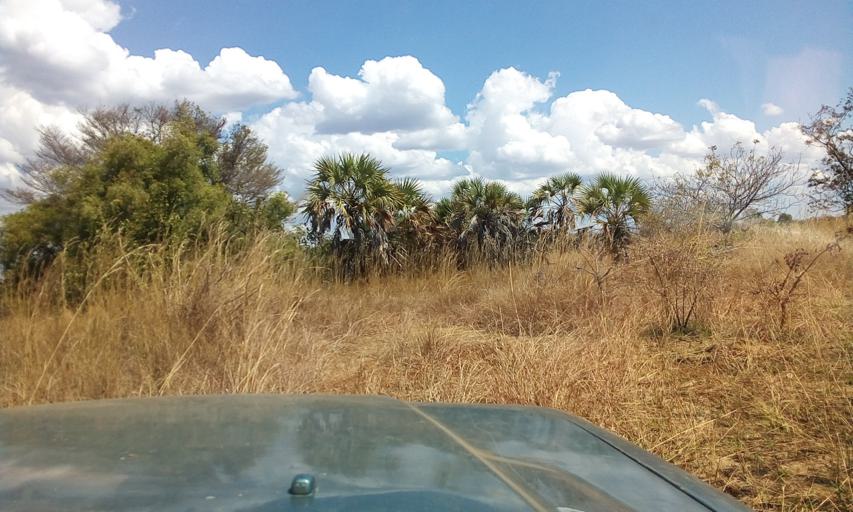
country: MG
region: Melaky
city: Mahabe
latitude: -16.4380
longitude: 45.3760
